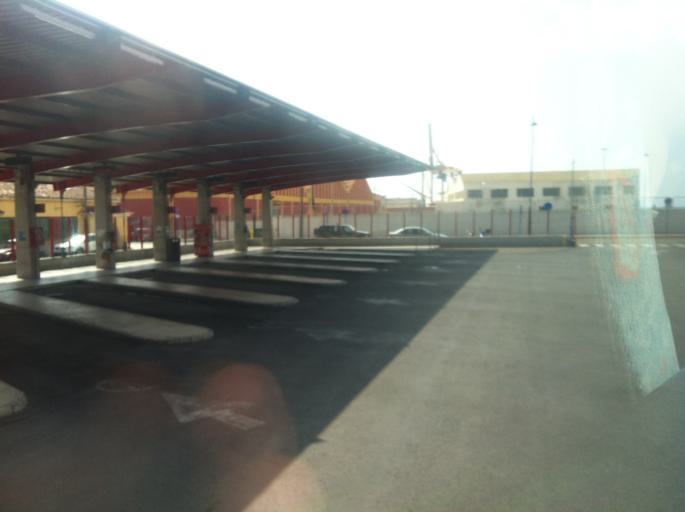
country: ES
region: Valencia
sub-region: Provincia de Alicante
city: Alicante
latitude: 38.3375
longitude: -0.4913
